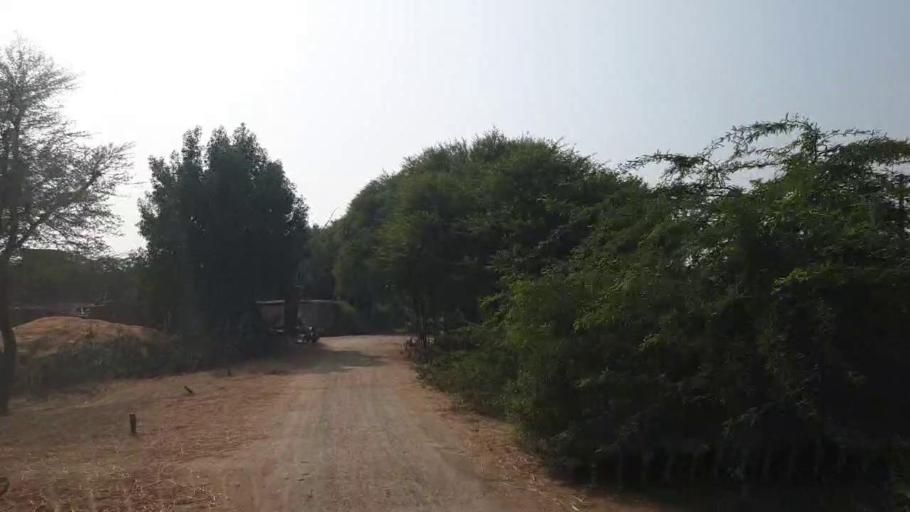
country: PK
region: Sindh
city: Rajo Khanani
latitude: 25.0318
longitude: 68.7778
